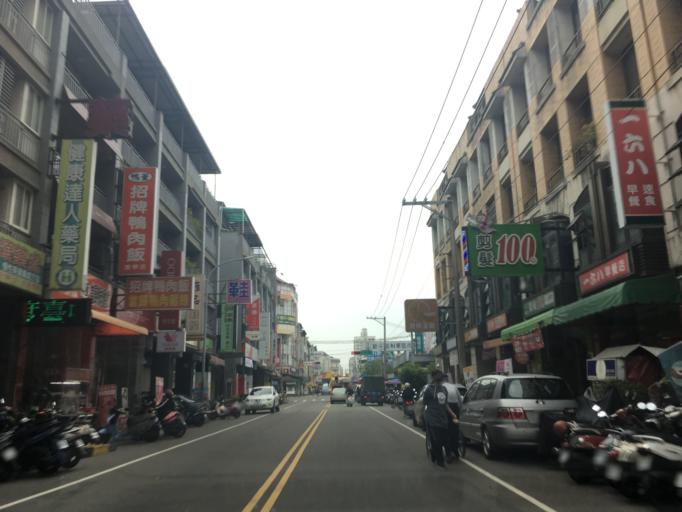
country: TW
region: Taiwan
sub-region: Taichung City
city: Taichung
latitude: 24.1753
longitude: 120.6968
